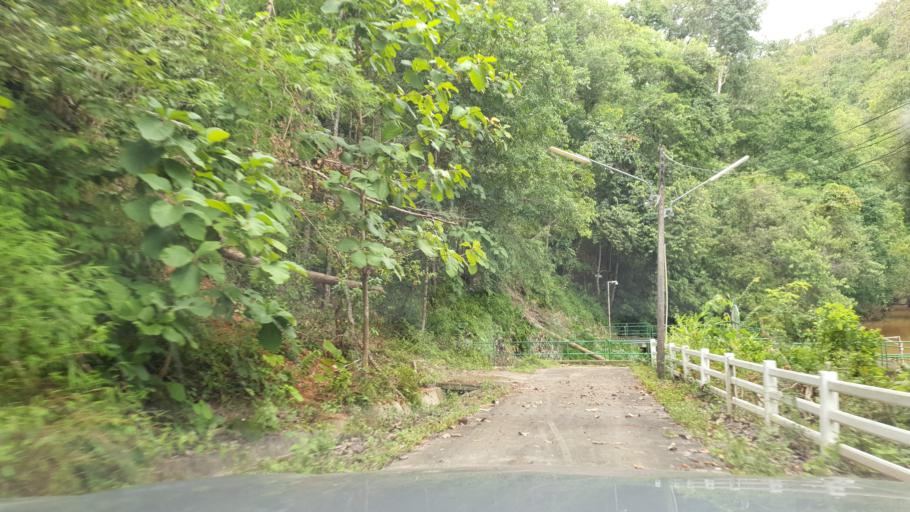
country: TH
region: Chiang Mai
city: Mae Wang
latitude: 18.6836
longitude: 98.6257
